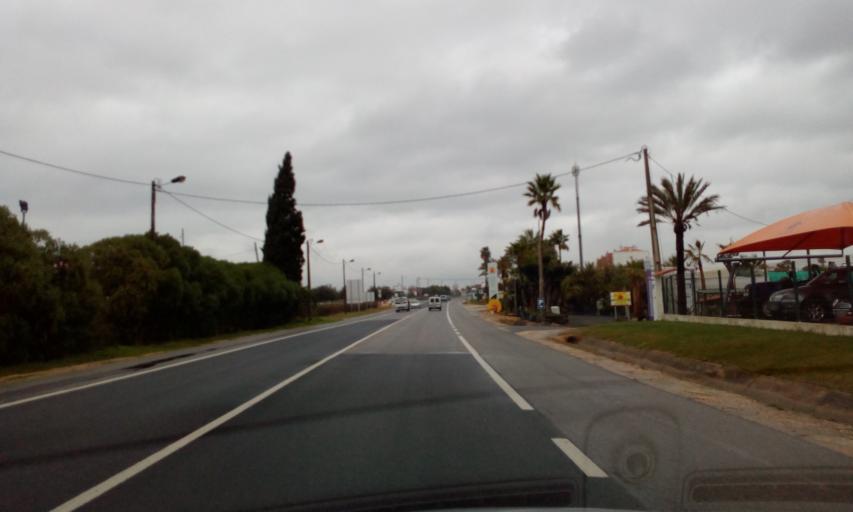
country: PT
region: Faro
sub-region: Lagos
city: Lagos
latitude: 37.1436
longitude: -8.6618
